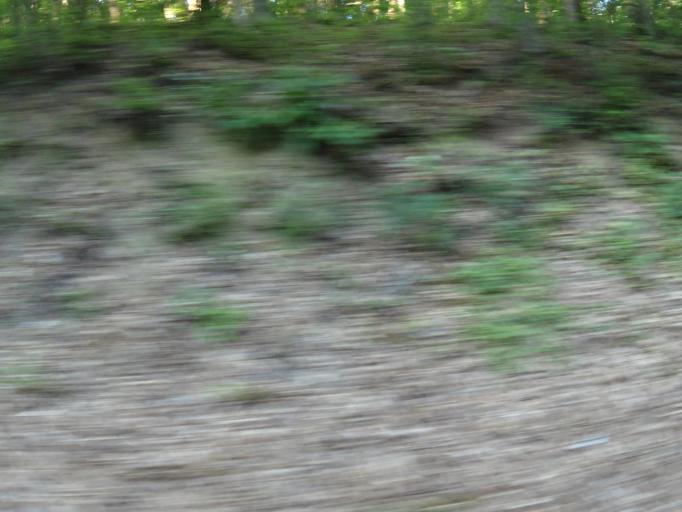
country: US
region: Tennessee
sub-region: Sevier County
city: Pigeon Forge
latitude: 35.8230
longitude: -83.5987
